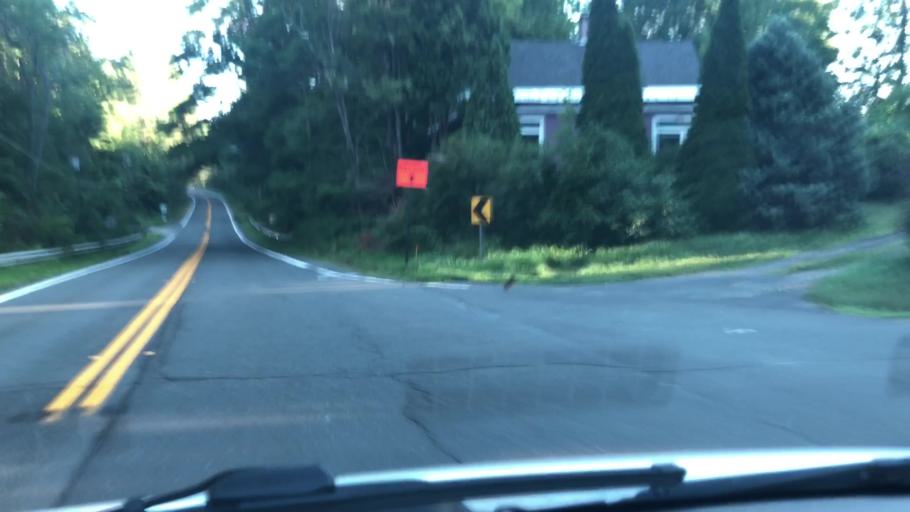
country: US
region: Massachusetts
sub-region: Hampshire County
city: Chesterfield
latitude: 42.3695
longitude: -72.9102
